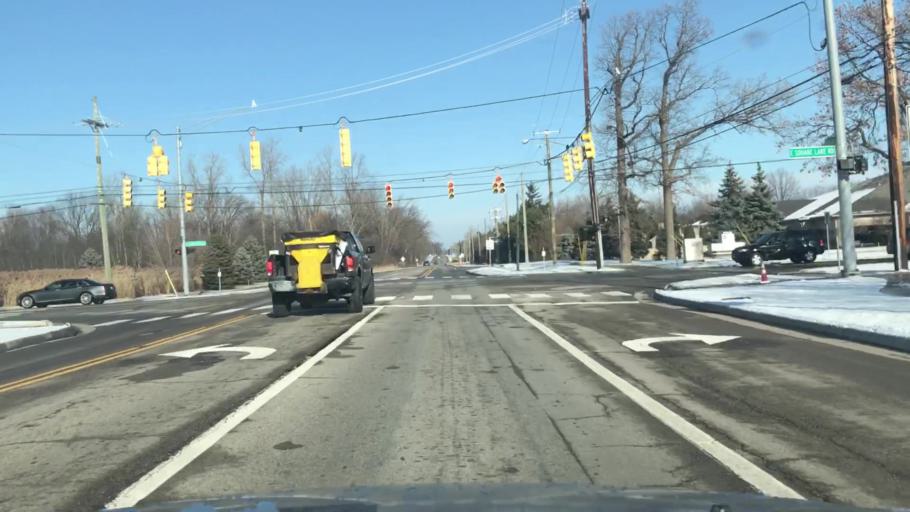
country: US
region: Michigan
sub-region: Oakland County
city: Troy
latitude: 42.6071
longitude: -83.1101
